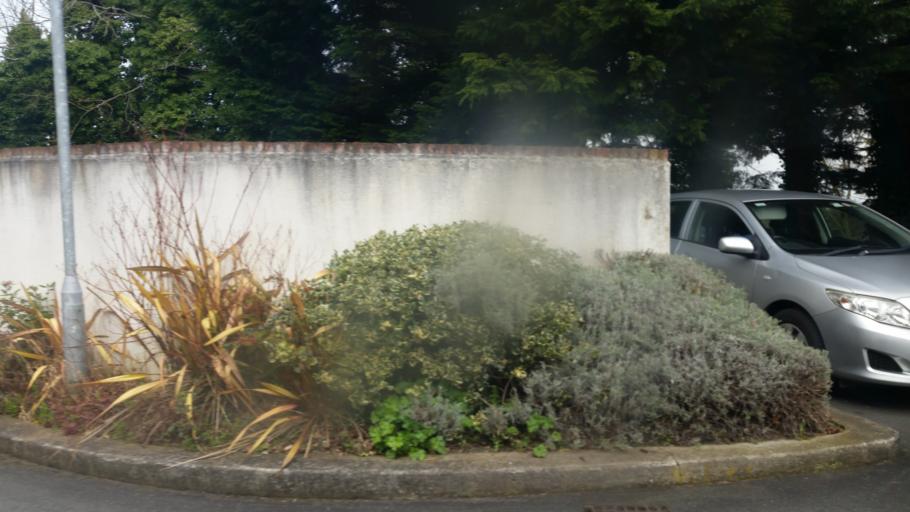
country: IE
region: Leinster
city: Portmarnock
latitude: 53.4199
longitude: -6.1508
